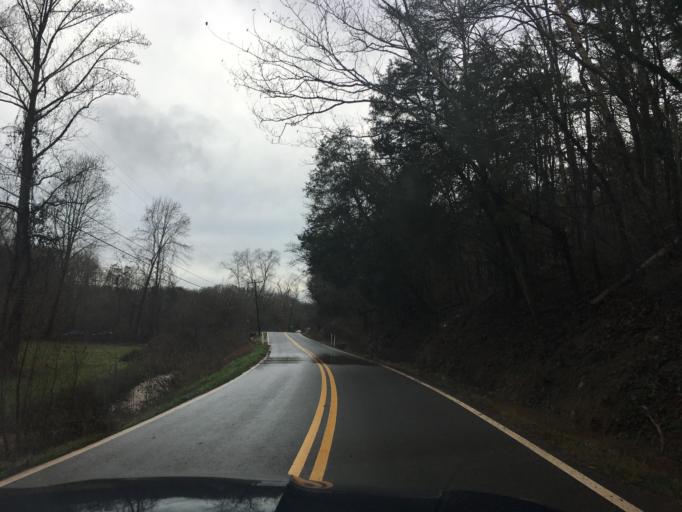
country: US
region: Tennessee
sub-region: McMinn County
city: Englewood
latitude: 35.4039
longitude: -84.4489
